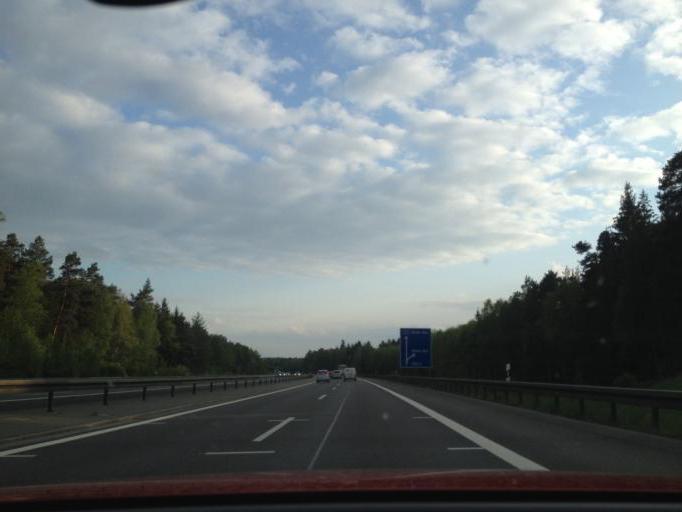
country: DE
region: Bavaria
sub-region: Upper Palatinate
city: Weiden
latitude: 49.7073
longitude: 12.1397
